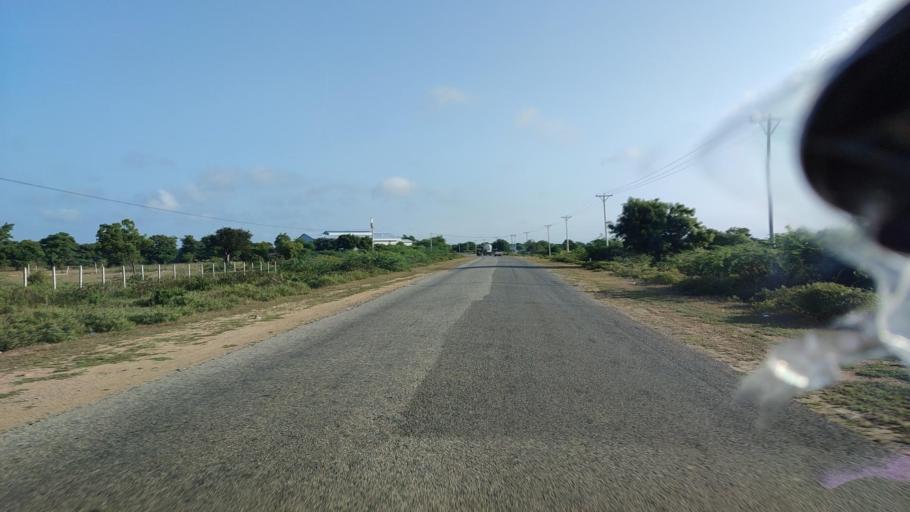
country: MM
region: Mandalay
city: Yamethin
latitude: 20.6200
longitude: 96.0793
